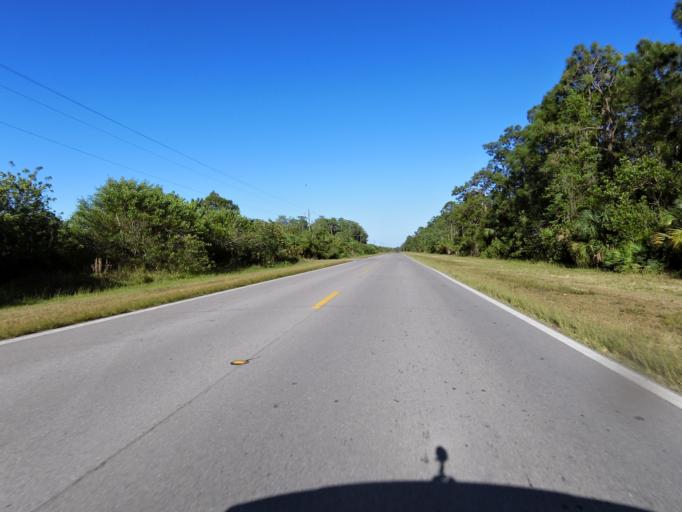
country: US
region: Florida
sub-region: Collier County
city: Immokalee
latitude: 26.2953
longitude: -81.3845
